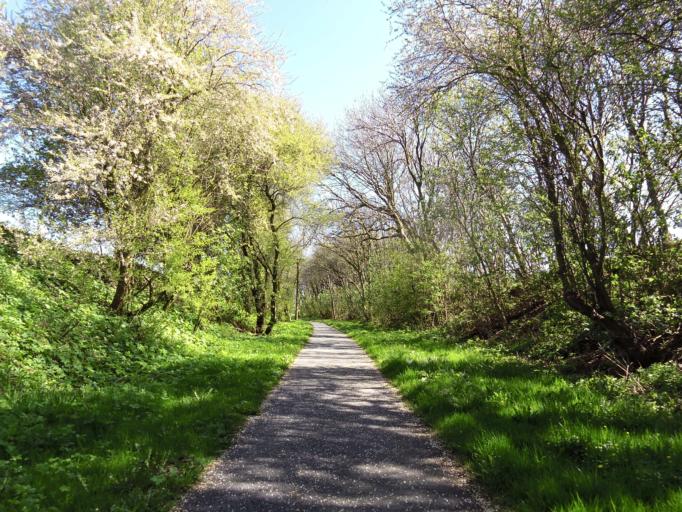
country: DK
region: Central Jutland
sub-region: Holstebro Kommune
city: Vinderup
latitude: 56.5954
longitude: 8.7784
